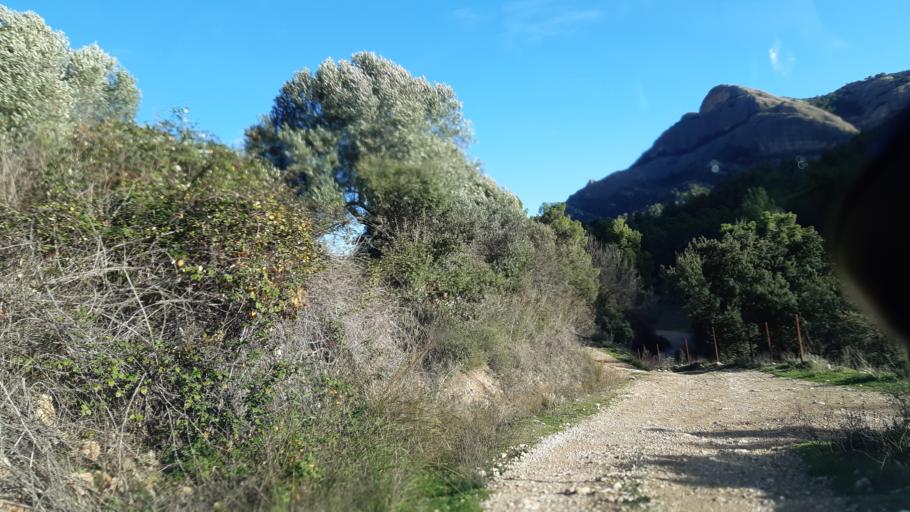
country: ES
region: Aragon
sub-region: Provincia de Teruel
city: Lledo
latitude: 40.8641
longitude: 0.2526
